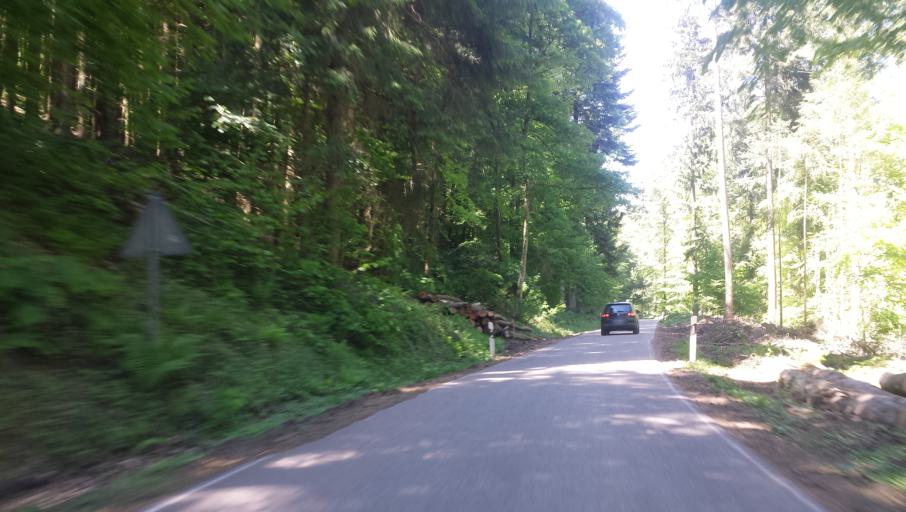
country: DE
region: Rheinland-Pfalz
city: Ramberg
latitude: 49.2742
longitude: 8.0286
